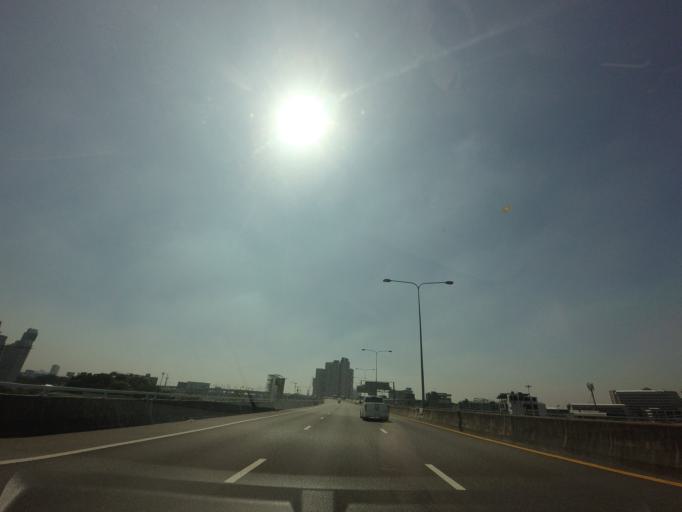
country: TH
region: Bangkok
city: Phra Khanong
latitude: 13.6787
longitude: 100.6039
